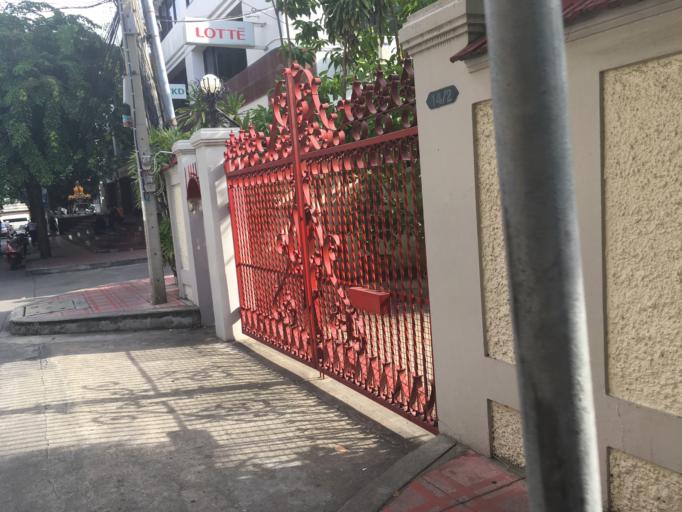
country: TH
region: Bangkok
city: Bang Rak
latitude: 13.7264
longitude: 100.5417
